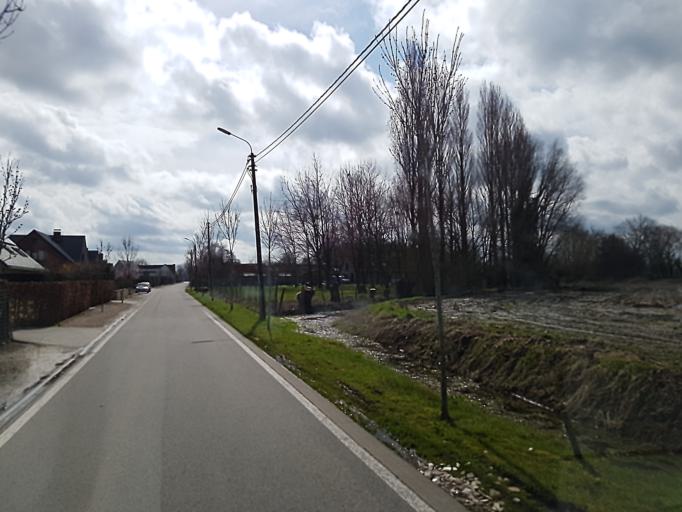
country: BE
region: Flanders
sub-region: Provincie Oost-Vlaanderen
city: Deinze
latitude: 50.9450
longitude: 3.4966
